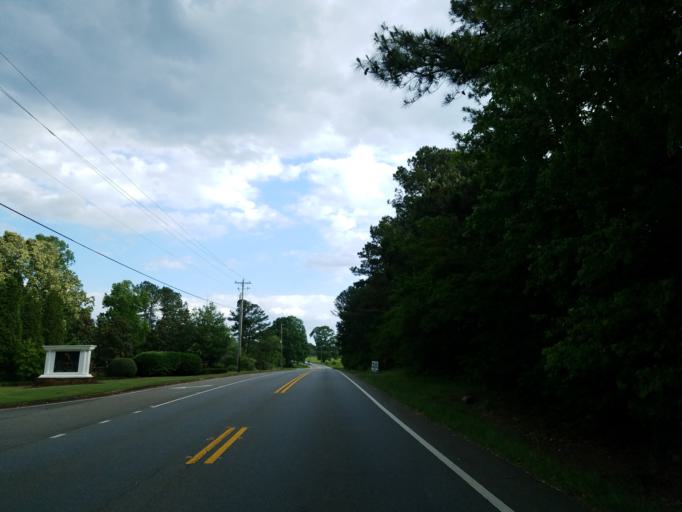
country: US
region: Georgia
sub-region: Cherokee County
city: Ball Ground
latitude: 34.2616
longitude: -84.2882
